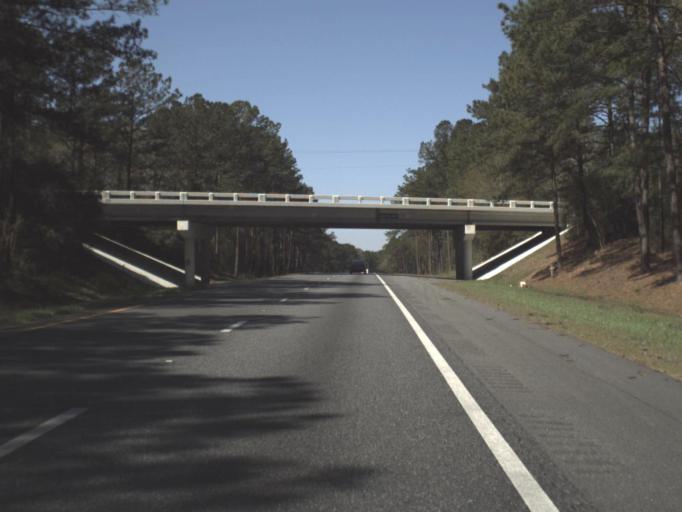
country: US
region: Florida
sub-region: Walton County
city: DeFuniak Springs
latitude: 30.6919
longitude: -86.0186
